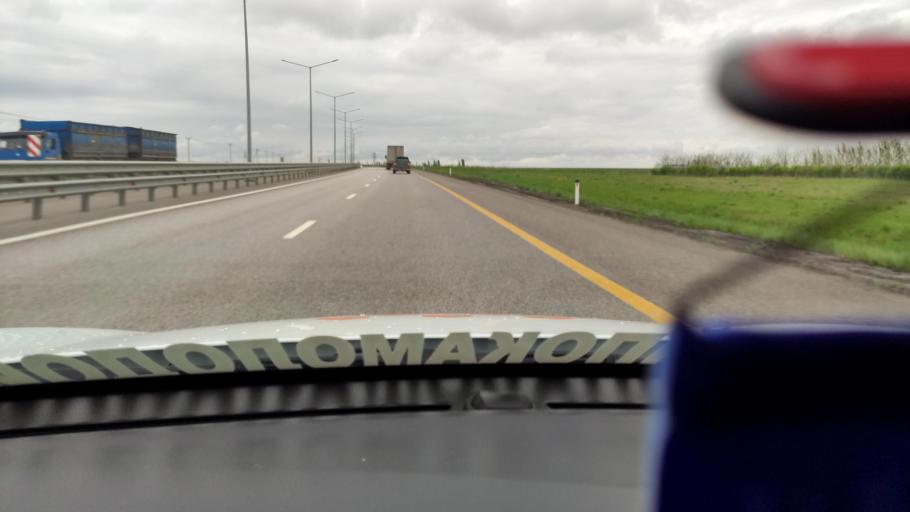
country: RU
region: Voronezj
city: Novaya Usman'
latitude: 51.5930
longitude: 39.3638
